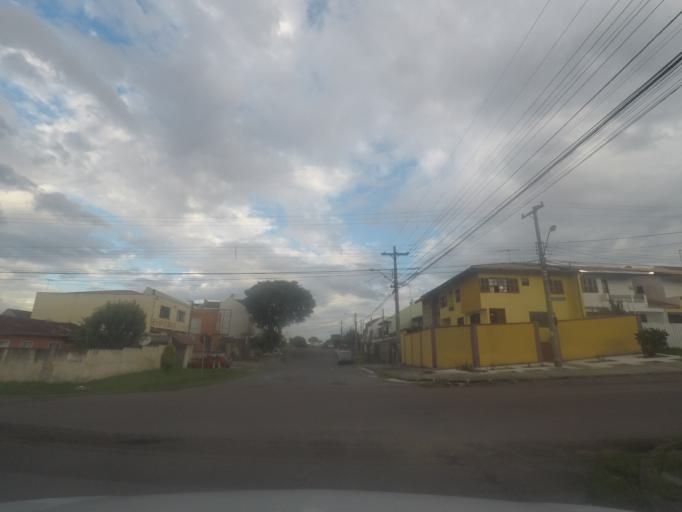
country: BR
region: Parana
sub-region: Pinhais
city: Pinhais
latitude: -25.4651
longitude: -49.2214
